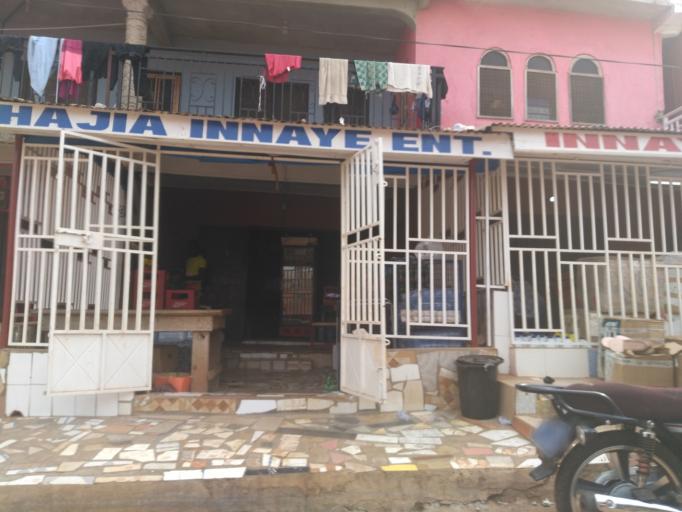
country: GH
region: Ashanti
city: Kumasi
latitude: 6.6947
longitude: -1.6140
